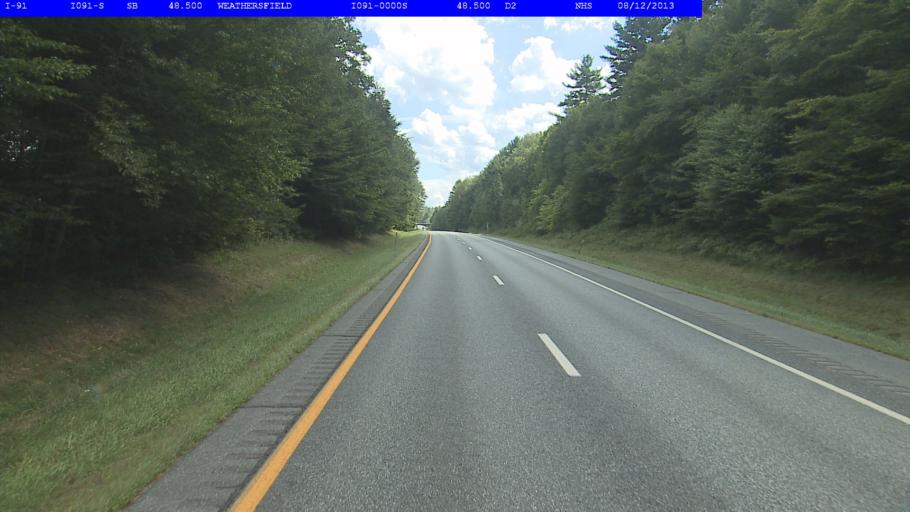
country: US
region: New Hampshire
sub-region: Sullivan County
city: Claremont
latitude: 43.3622
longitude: -72.4251
